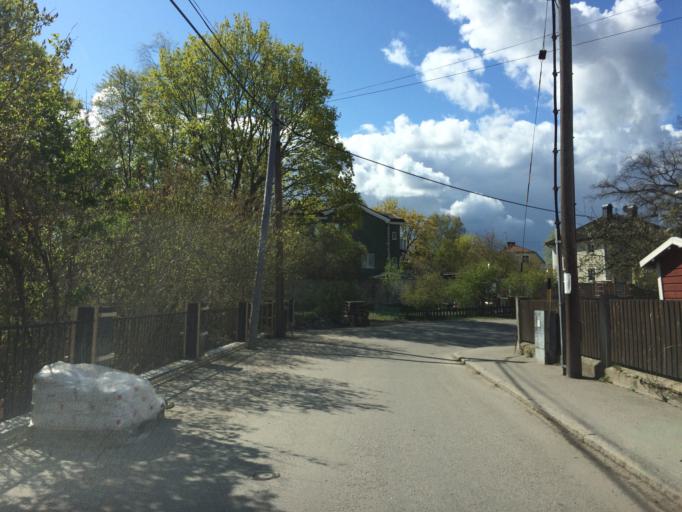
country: SE
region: Stockholm
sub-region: Huddinge Kommun
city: Segeltorp
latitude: 59.3015
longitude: 17.9654
